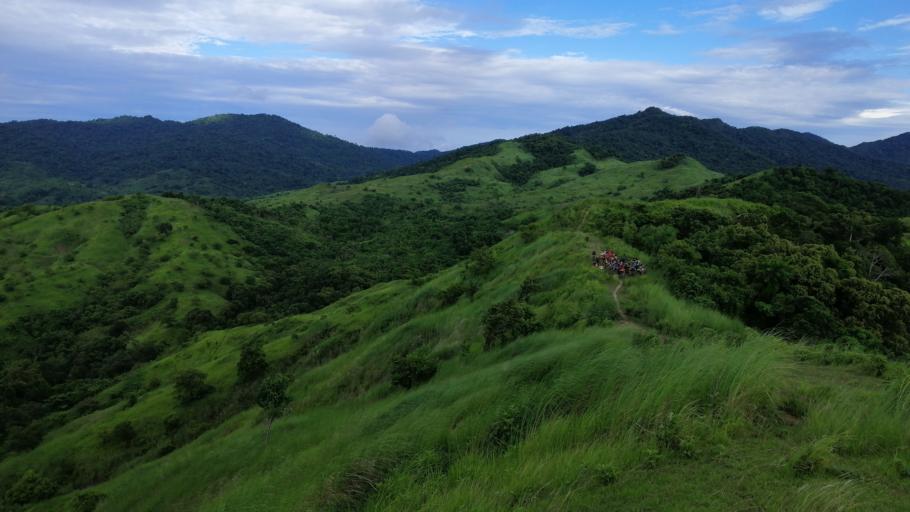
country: PH
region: Central Luzon
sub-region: Province of Bulacan
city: Sibul
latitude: 15.1473
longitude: 121.1397
